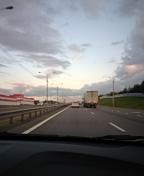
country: RU
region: Moskovskaya
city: Vereya
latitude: 55.5531
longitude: 38.0663
